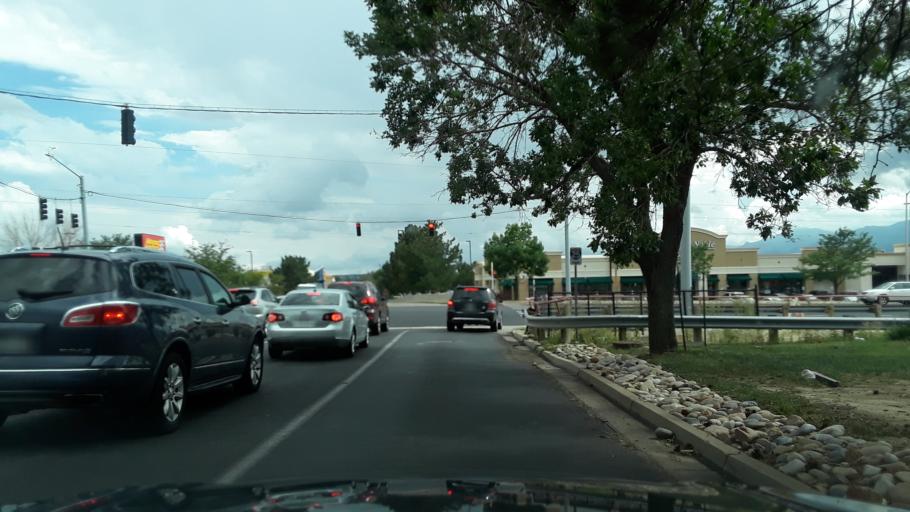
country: US
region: Colorado
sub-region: El Paso County
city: Air Force Academy
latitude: 38.9458
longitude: -104.7983
